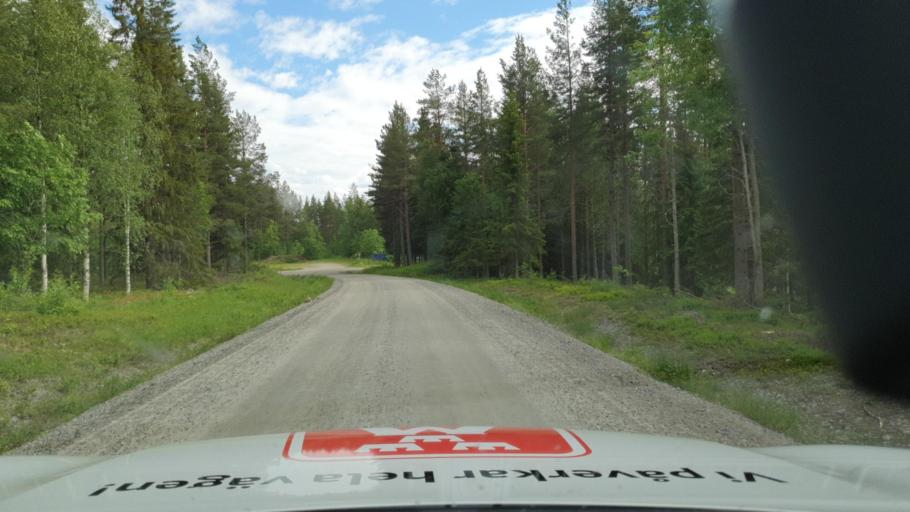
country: SE
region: Vaesterbotten
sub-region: Norsjo Kommun
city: Norsjoe
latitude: 64.7883
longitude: 19.6563
